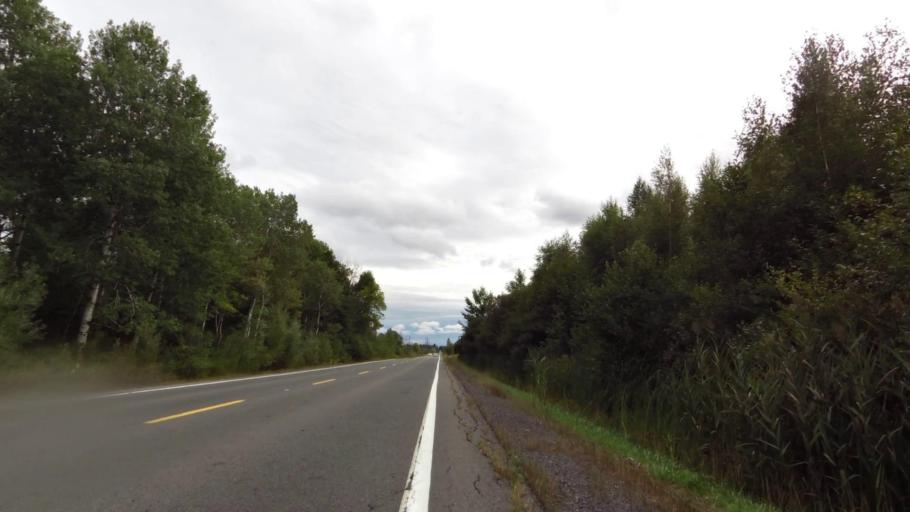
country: CA
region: Ontario
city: Ottawa
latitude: 45.2995
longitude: -75.6395
